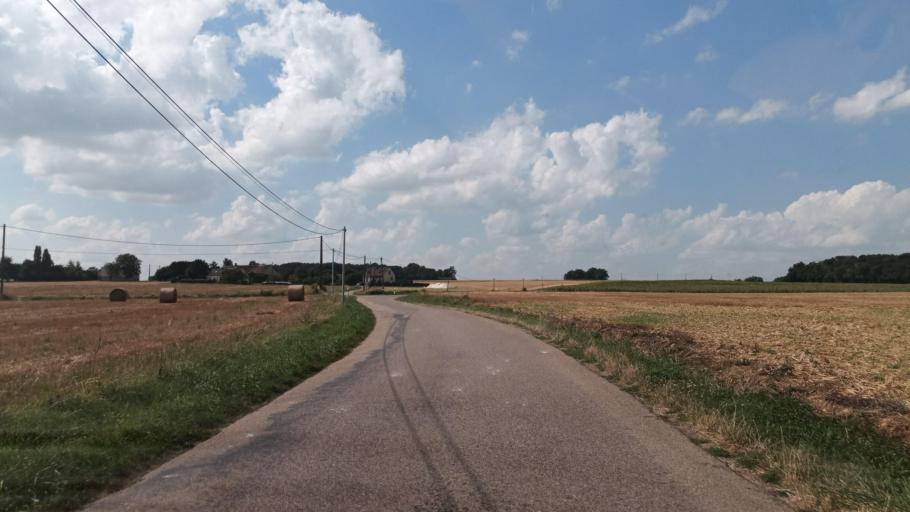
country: FR
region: Bourgogne
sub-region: Departement de l'Yonne
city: Egriselles-le-Bocage
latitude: 48.0291
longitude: 3.1681
